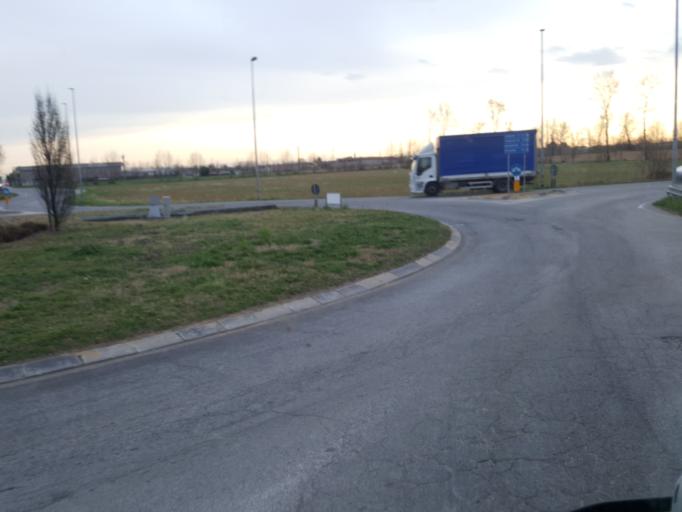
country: IT
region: Lombardy
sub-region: Provincia di Brescia
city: Duomo
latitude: 45.5480
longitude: 10.0120
